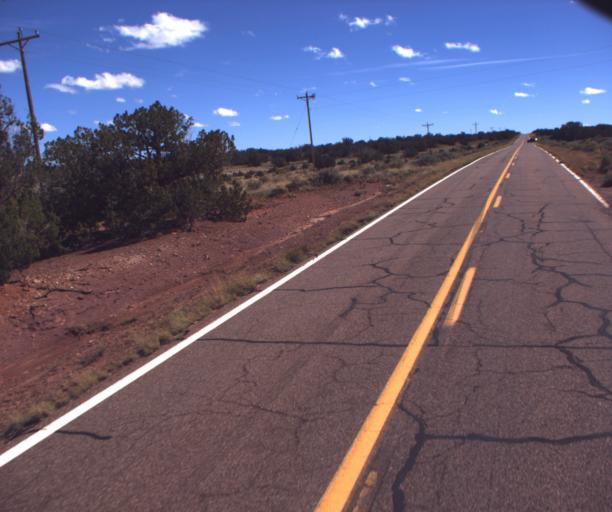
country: US
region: Arizona
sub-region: Apache County
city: Saint Johns
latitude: 34.5940
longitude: -109.6483
